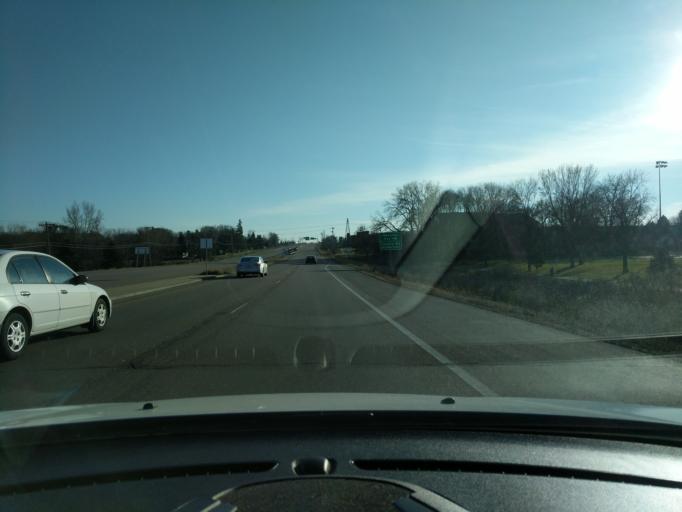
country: US
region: Minnesota
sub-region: Ramsey County
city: Roseville
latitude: 45.0202
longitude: -93.1671
